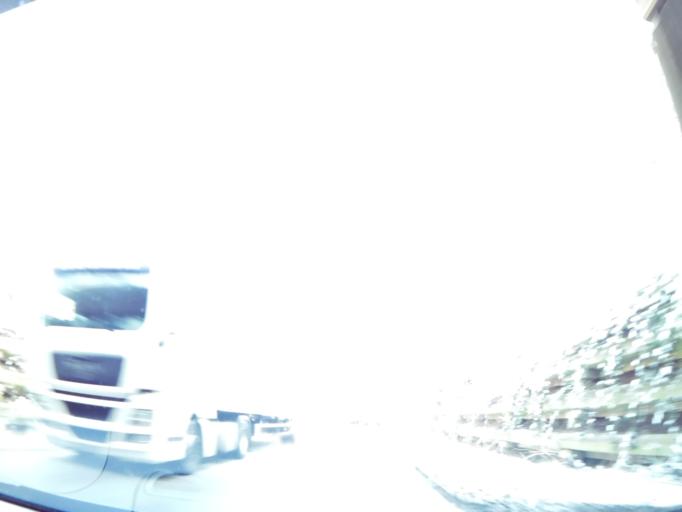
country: DE
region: North Rhine-Westphalia
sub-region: Regierungsbezirk Koln
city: Wurselen
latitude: 50.8280
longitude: 6.1373
